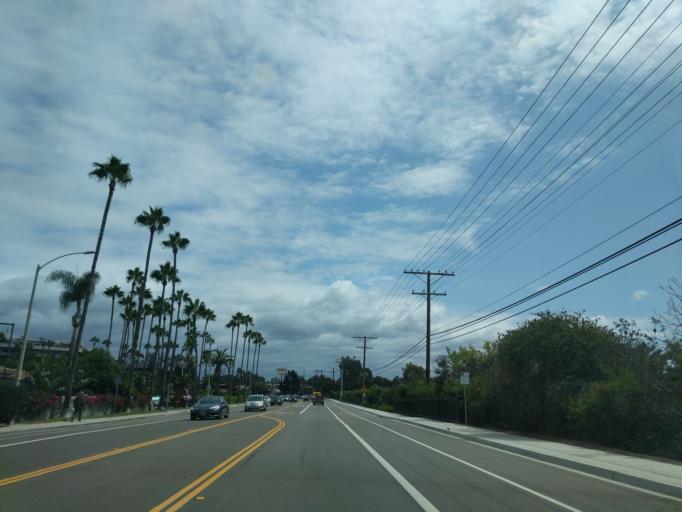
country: US
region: California
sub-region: San Diego County
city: Solana Beach
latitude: 32.9801
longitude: -117.2600
